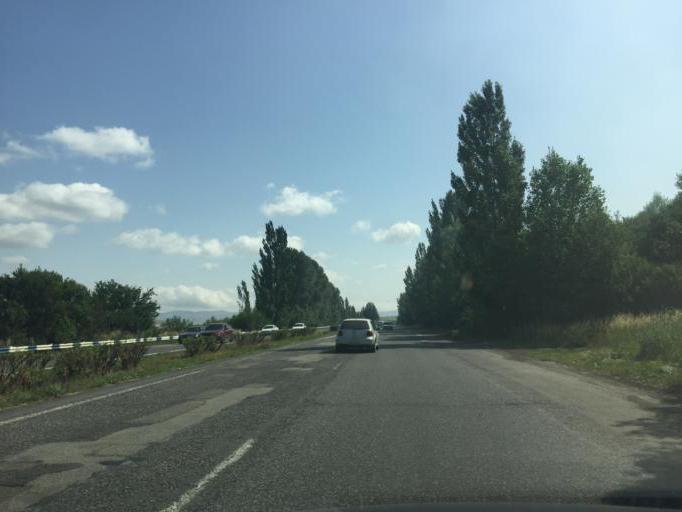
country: AM
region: Kotayk'i Marz
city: Hrazdan
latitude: 40.4781
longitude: 44.7558
